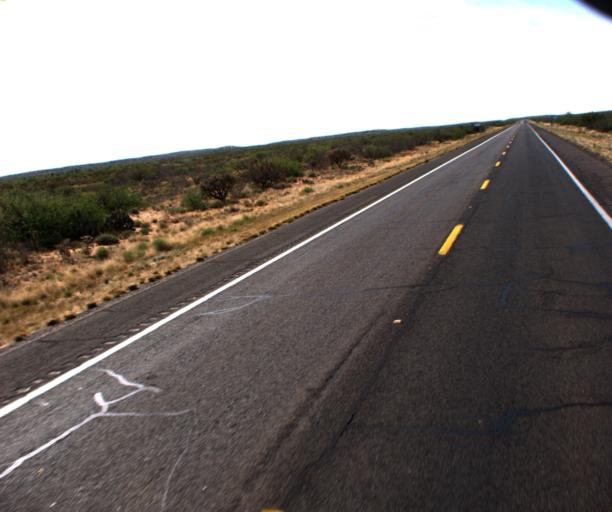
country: US
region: Arizona
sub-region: Graham County
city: Swift Trail Junction
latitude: 32.6646
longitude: -109.7018
